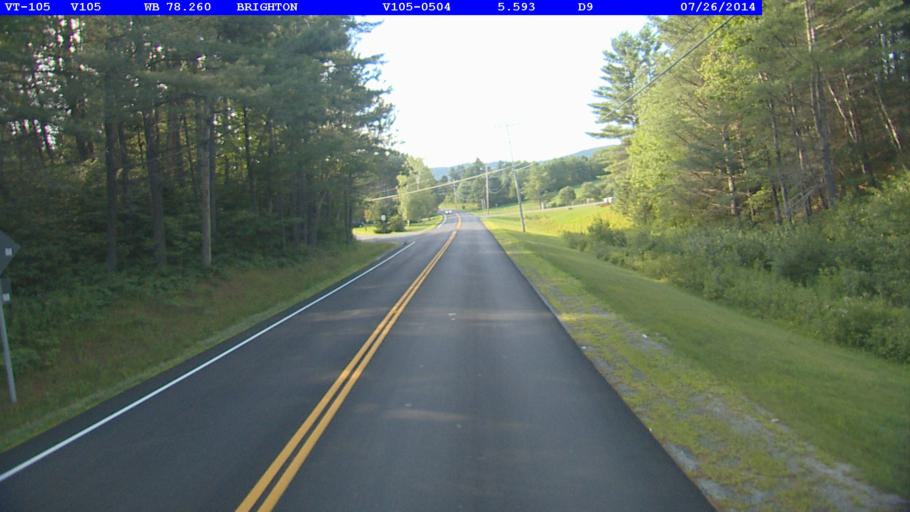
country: US
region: Vermont
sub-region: Caledonia County
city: Lyndonville
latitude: 44.8111
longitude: -71.8617
